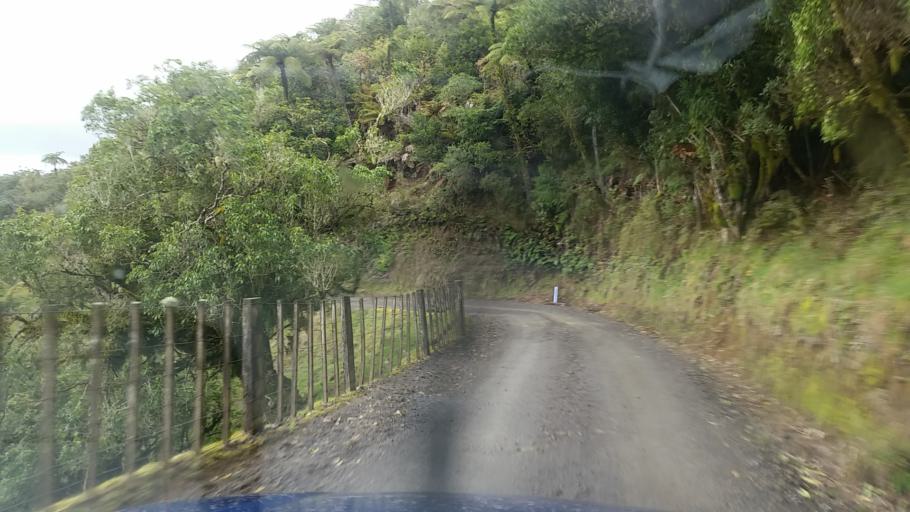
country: NZ
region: Taranaki
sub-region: South Taranaki District
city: Eltham
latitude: -39.1697
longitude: 174.6265
